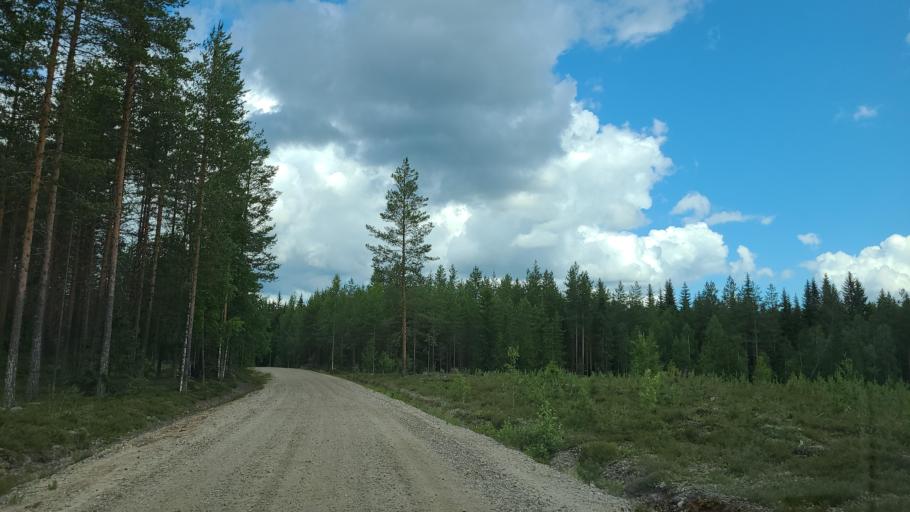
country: FI
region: Northern Savo
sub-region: Koillis-Savo
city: Kaavi
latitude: 63.0474
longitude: 28.8170
